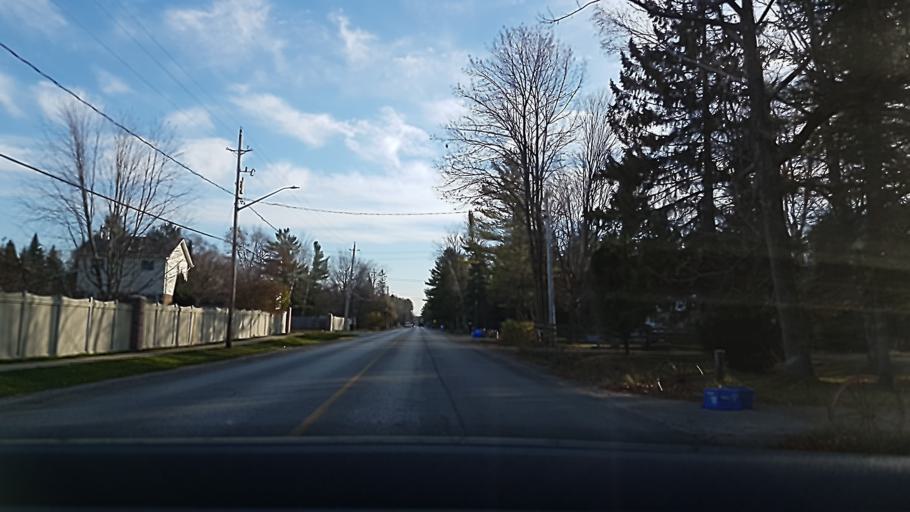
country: CA
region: Ontario
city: Innisfil
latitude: 44.3334
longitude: -79.5441
